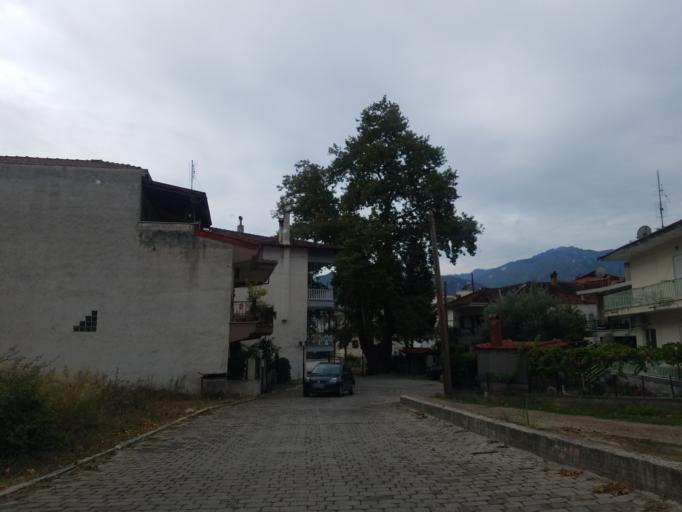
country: GR
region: Thessaly
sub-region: Trikala
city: Kalampaka
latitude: 39.7088
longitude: 21.6298
